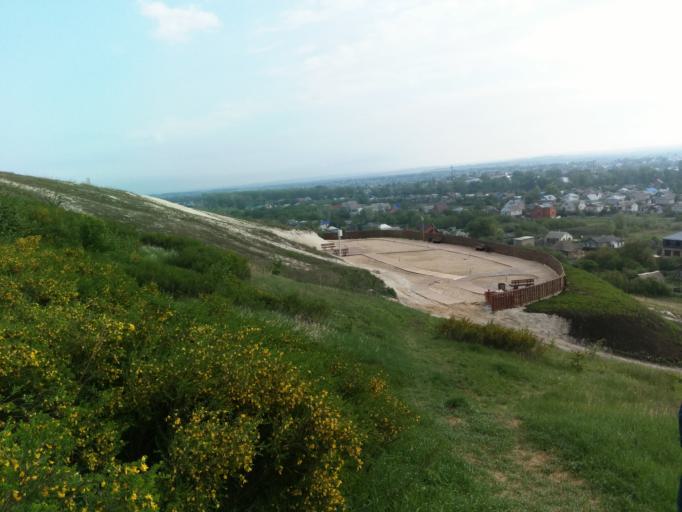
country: RU
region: Voronezj
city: Kalach
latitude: 50.4155
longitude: 41.0051
